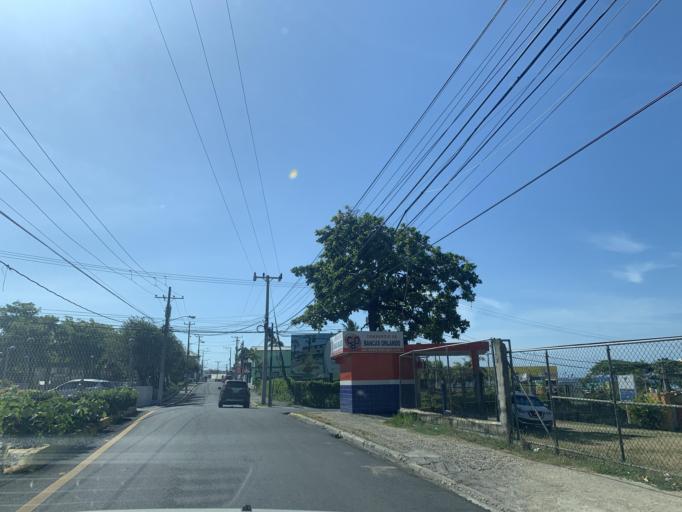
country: DO
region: Puerto Plata
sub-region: Puerto Plata
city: Puerto Plata
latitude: 19.7938
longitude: -70.6839
